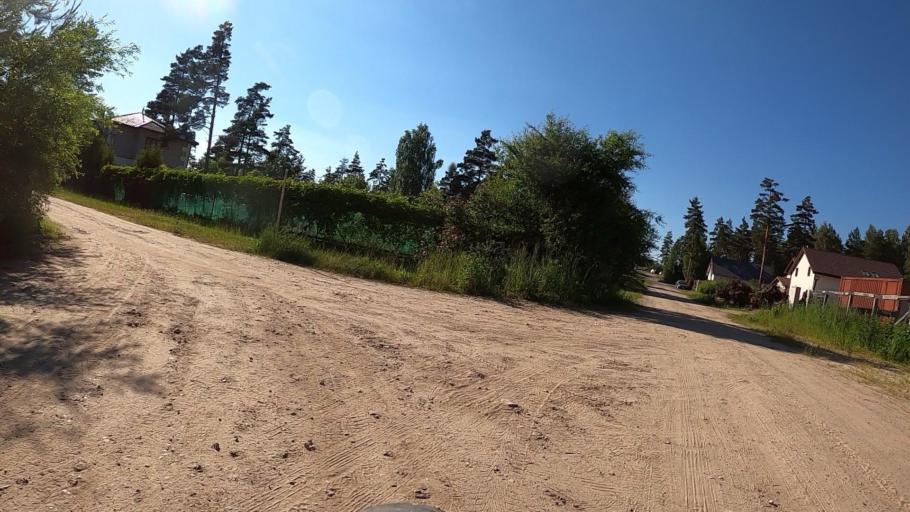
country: LV
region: Stopini
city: Ulbroka
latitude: 56.8791
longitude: 24.2995
